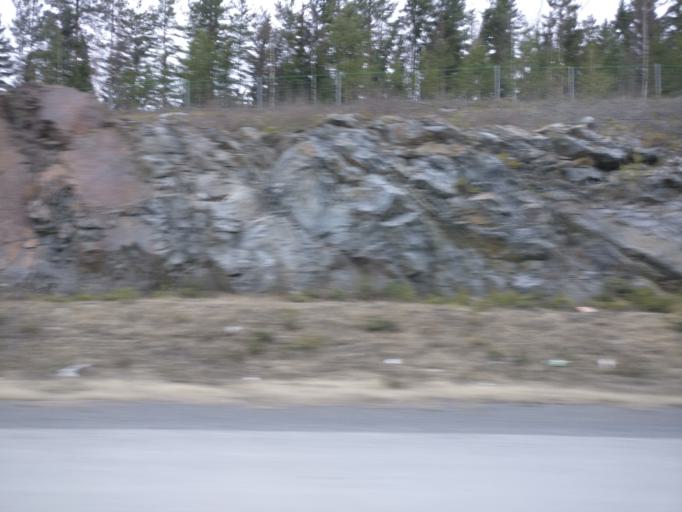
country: FI
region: Pirkanmaa
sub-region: Etelae-Pirkanmaa
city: Toijala
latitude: 61.2404
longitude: 23.8375
